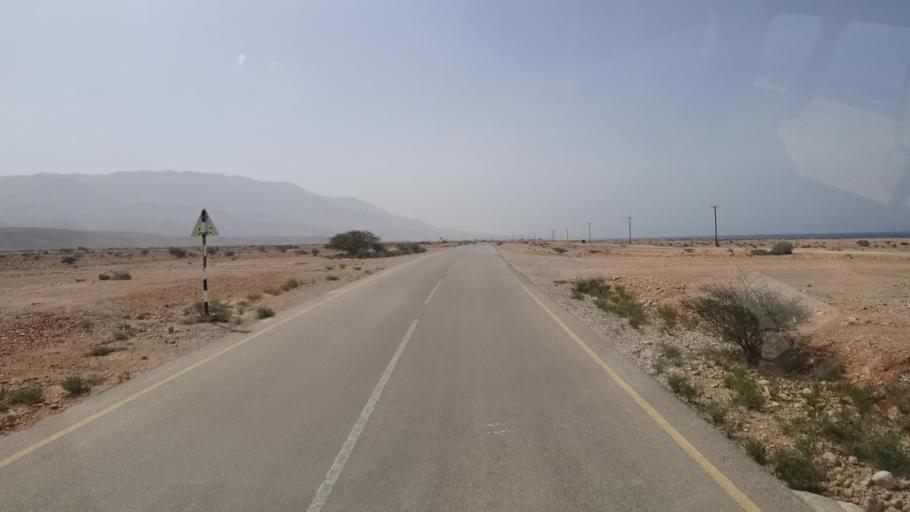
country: OM
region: Ash Sharqiyah
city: Sur
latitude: 22.9792
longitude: 59.1553
